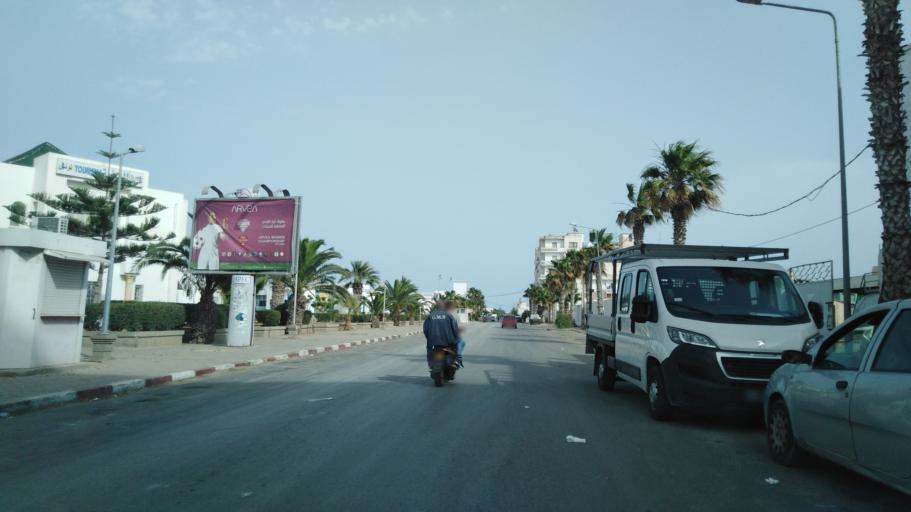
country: TN
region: Safaqis
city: Sfax
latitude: 34.7289
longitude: 10.7609
